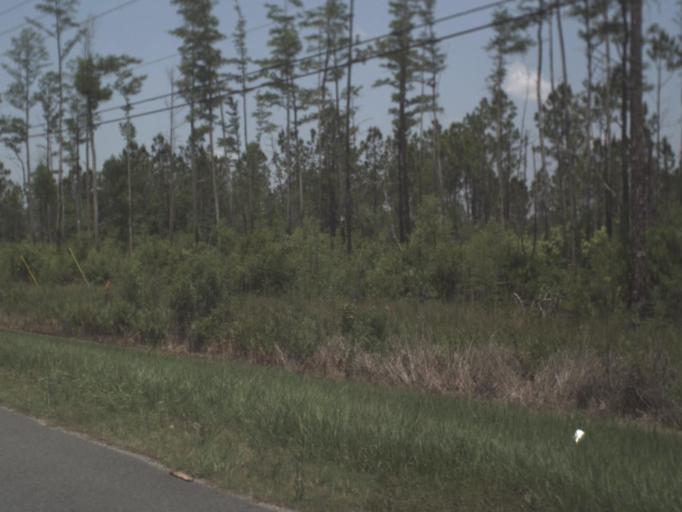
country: US
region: Florida
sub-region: Duval County
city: Baldwin
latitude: 30.2035
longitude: -81.9959
